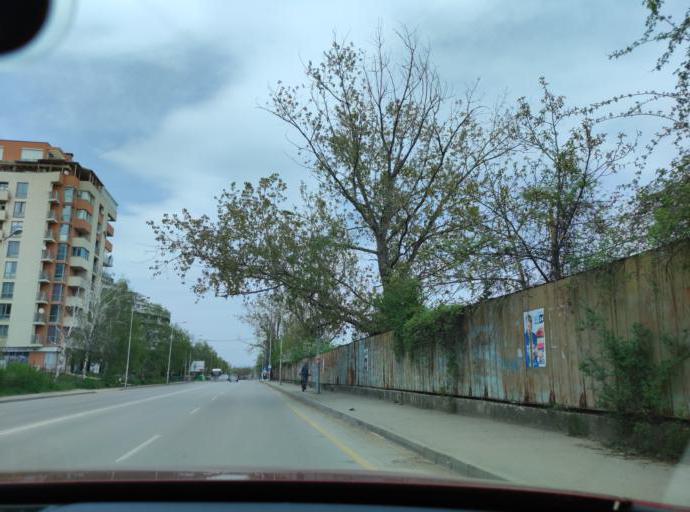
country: BG
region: Sofia-Capital
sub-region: Stolichna Obshtina
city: Sofia
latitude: 42.6481
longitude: 23.3459
